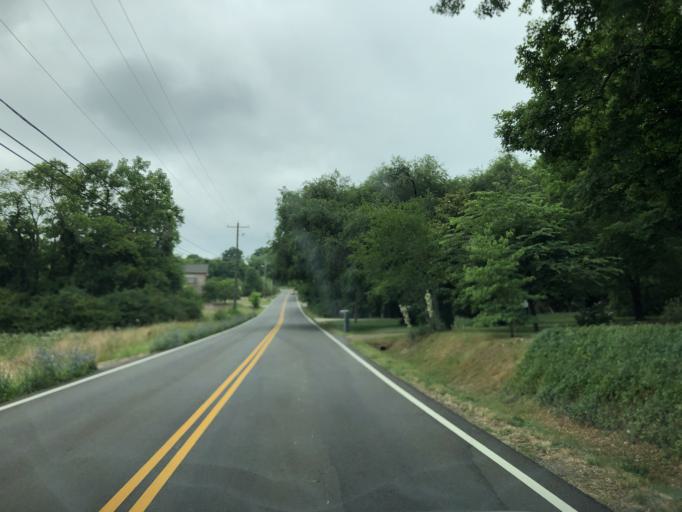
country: US
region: Tennessee
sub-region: Davidson County
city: Goodlettsville
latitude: 36.2947
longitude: -86.7500
